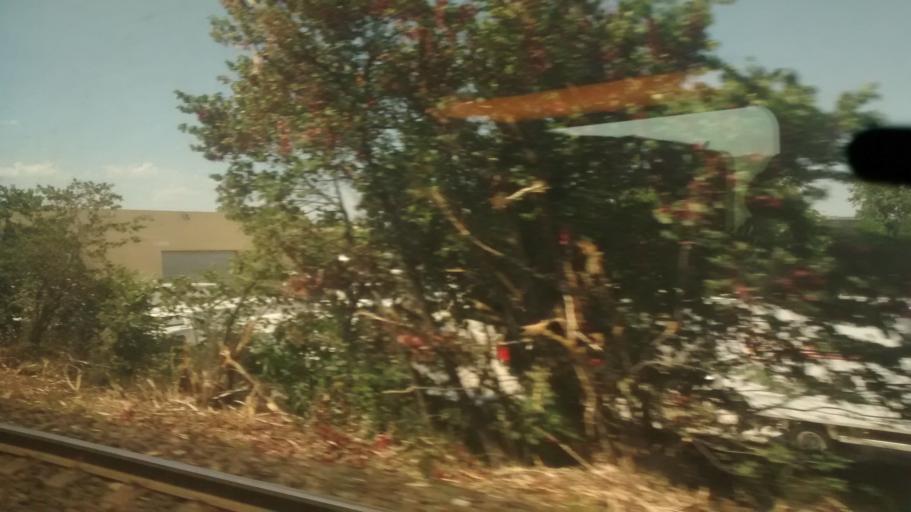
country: FR
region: Languedoc-Roussillon
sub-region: Departement de l'Herault
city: Le Cres
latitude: 43.6394
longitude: 3.9455
